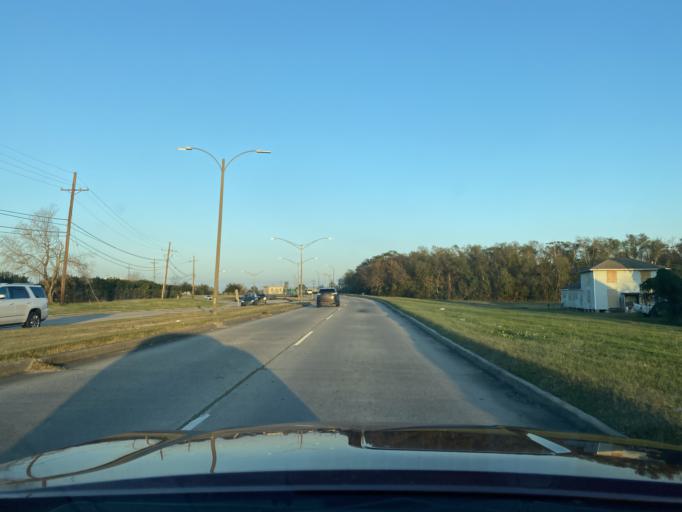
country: US
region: Louisiana
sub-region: Orleans Parish
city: New Orleans
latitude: 30.0268
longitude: -90.0490
